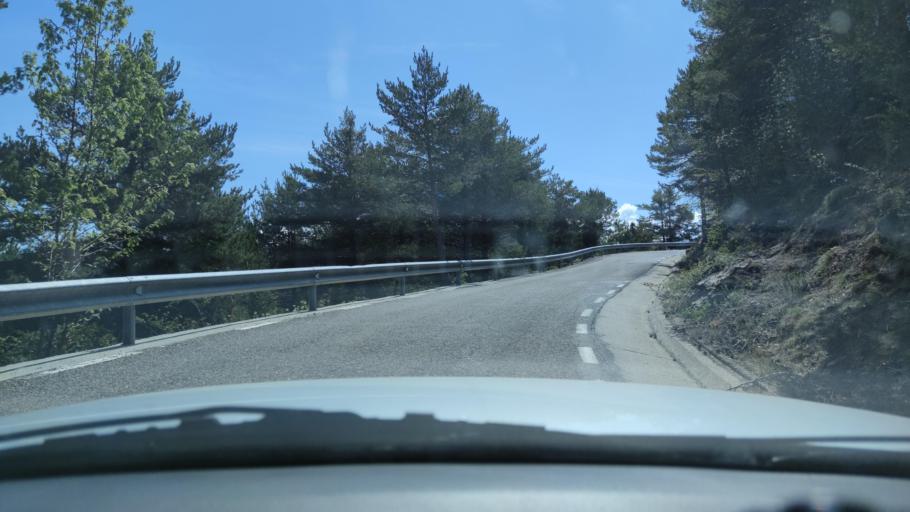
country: ES
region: Catalonia
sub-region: Provincia de Lleida
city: Coll de Nargo
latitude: 42.3116
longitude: 1.2811
